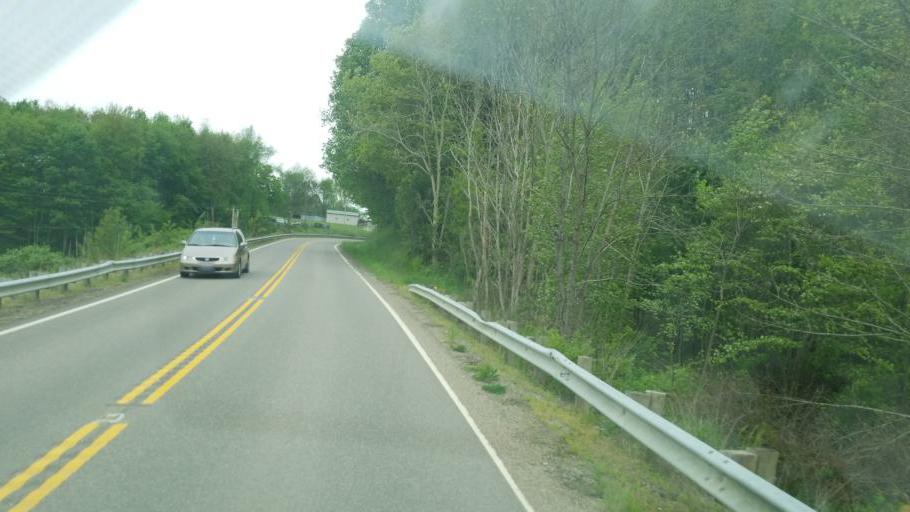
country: US
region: Ohio
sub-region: Tuscarawas County
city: Newcomerstown
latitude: 40.1868
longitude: -81.5311
